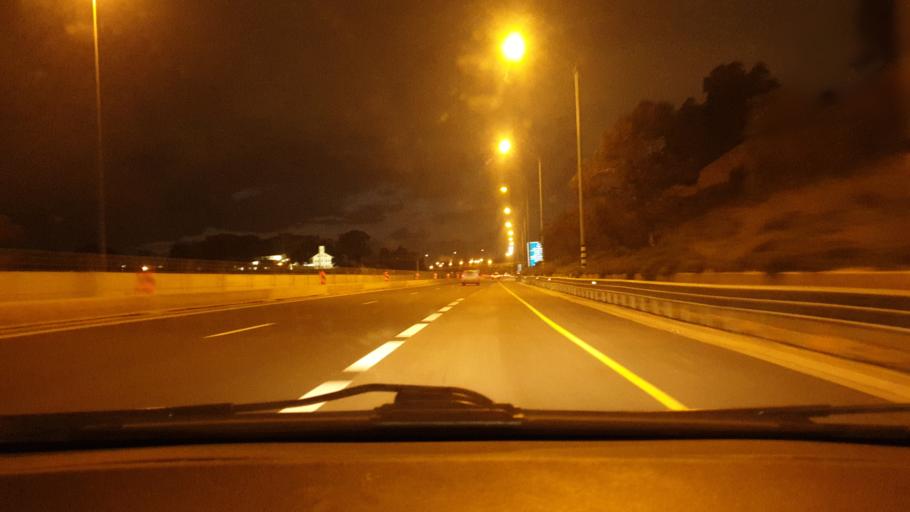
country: IL
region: Central District
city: Ramla
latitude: 31.9240
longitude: 34.8337
